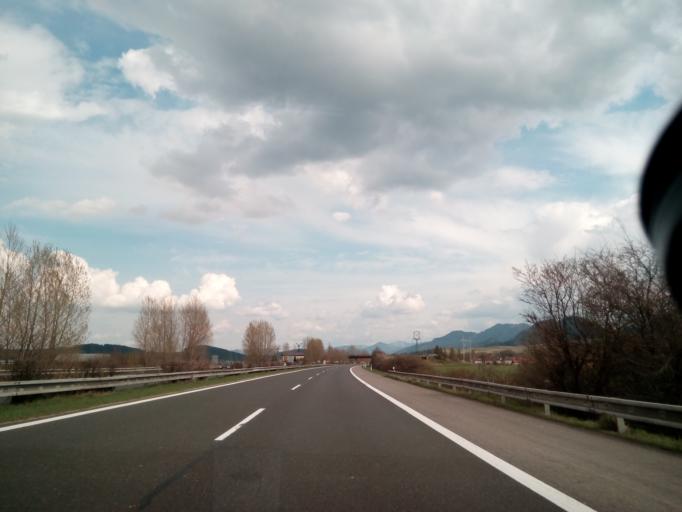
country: SK
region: Zilinsky
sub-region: Okres Liptovsky Mikulas
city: Liptovsky Mikulas
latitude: 49.0663
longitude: 19.6415
